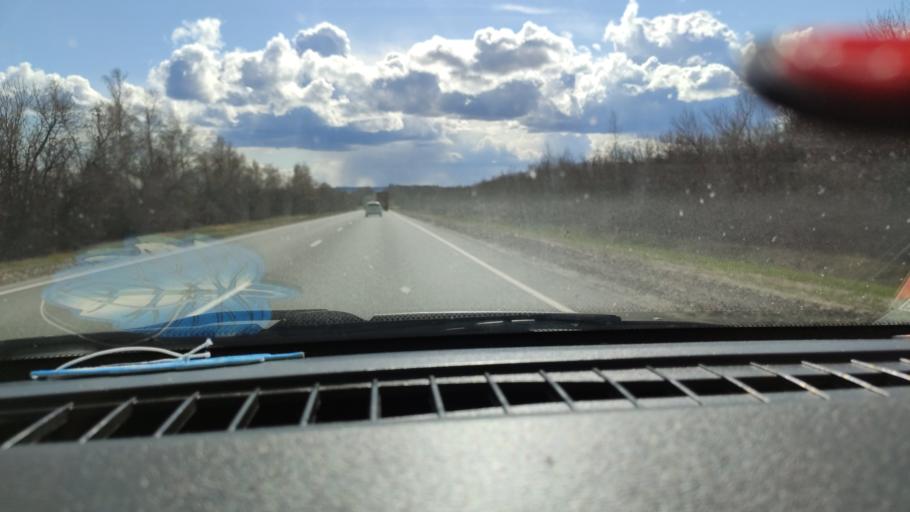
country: RU
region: Saratov
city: Khvalynsk
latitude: 52.6098
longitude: 48.1573
